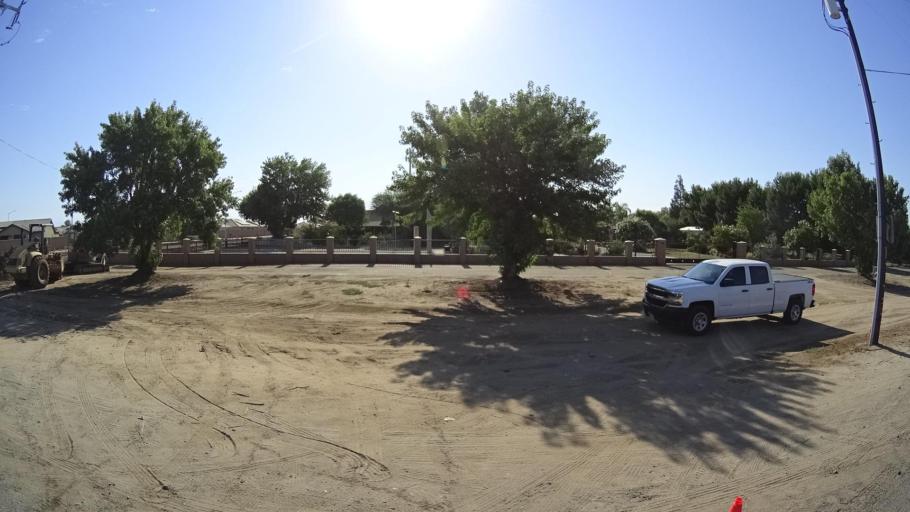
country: US
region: California
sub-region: Fresno County
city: Sunnyside
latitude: 36.7645
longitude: -119.6640
